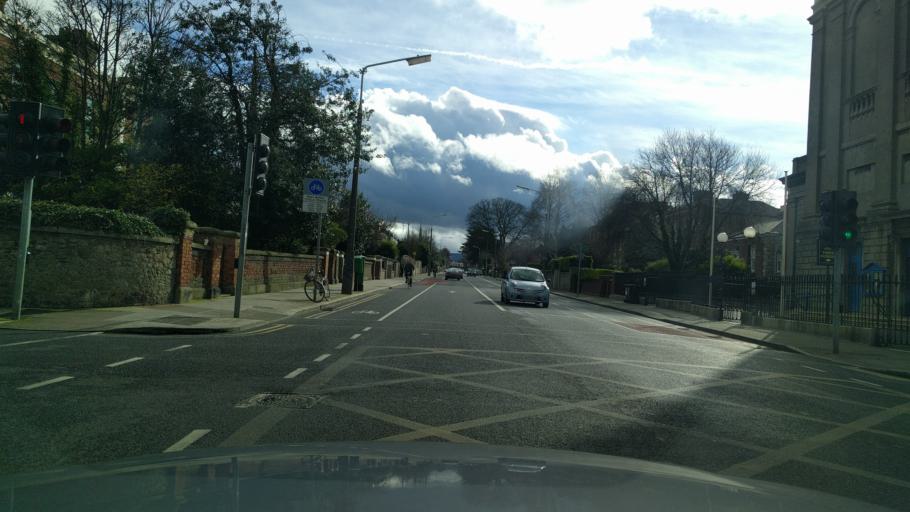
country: IE
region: Leinster
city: Rathgar
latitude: 53.3173
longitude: -6.2702
